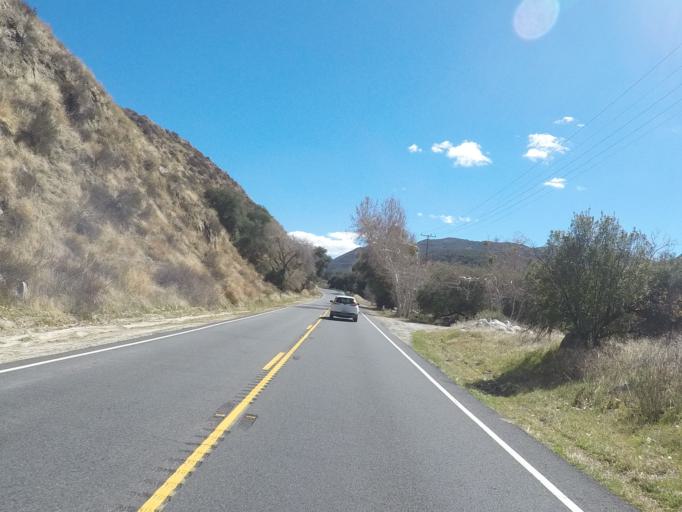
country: US
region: California
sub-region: Riverside County
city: Idyllwild-Pine Cove
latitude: 33.7260
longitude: -116.8061
